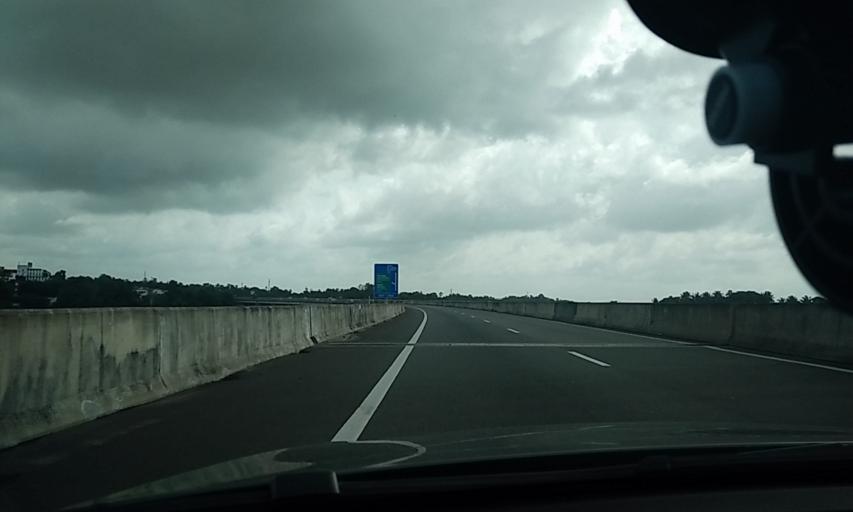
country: LK
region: Western
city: Mulleriyawa
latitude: 6.9134
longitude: 79.9826
